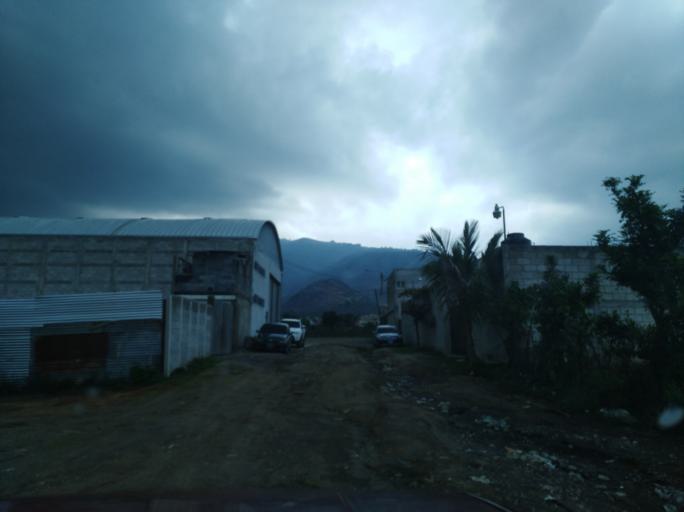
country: GT
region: Guatemala
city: Amatitlan
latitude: 14.5230
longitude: -90.6243
